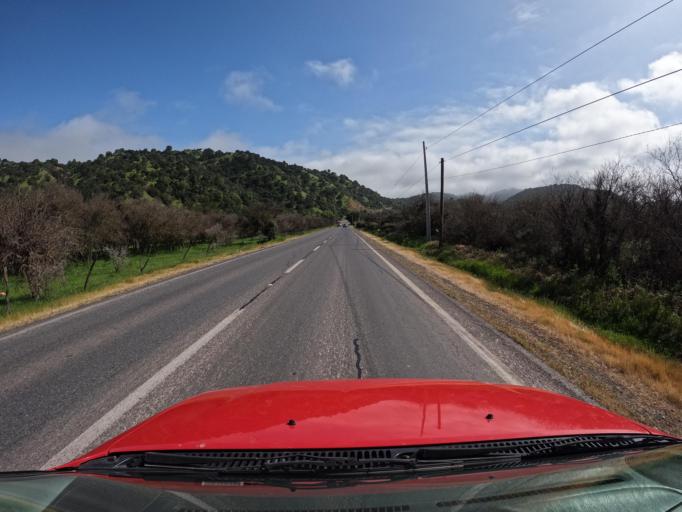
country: CL
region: Maule
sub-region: Provincia de Curico
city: Teno
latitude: -34.8263
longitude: -71.1916
